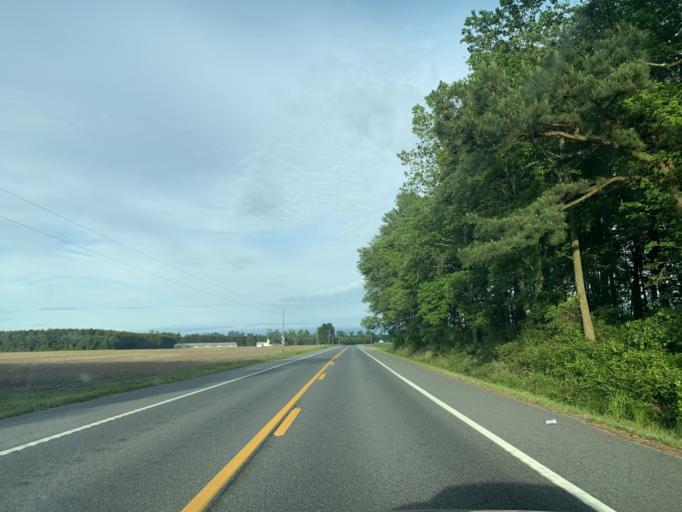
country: US
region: Virginia
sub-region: Accomack County
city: Captains Cove
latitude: 38.0699
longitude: -75.4505
